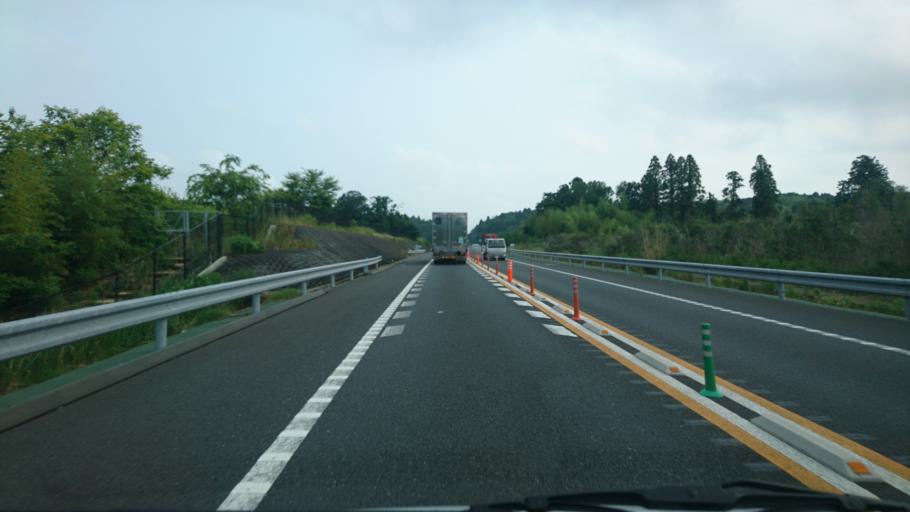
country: JP
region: Chiba
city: Narita
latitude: 35.8348
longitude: 140.3845
